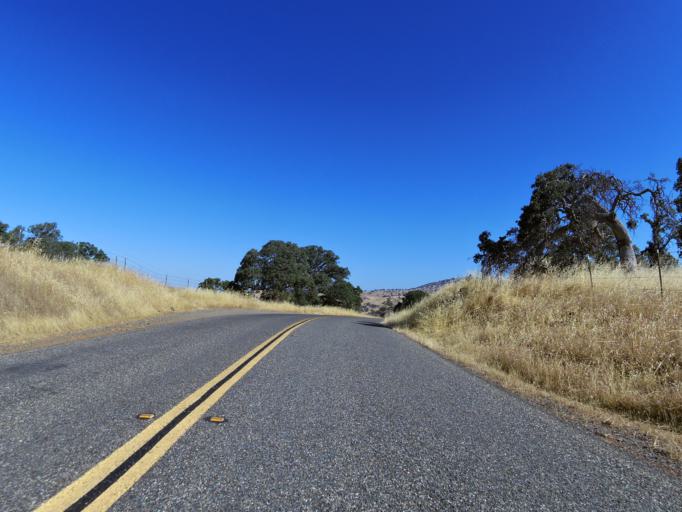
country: US
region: California
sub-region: Mariposa County
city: Mariposa
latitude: 37.4767
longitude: -120.1337
